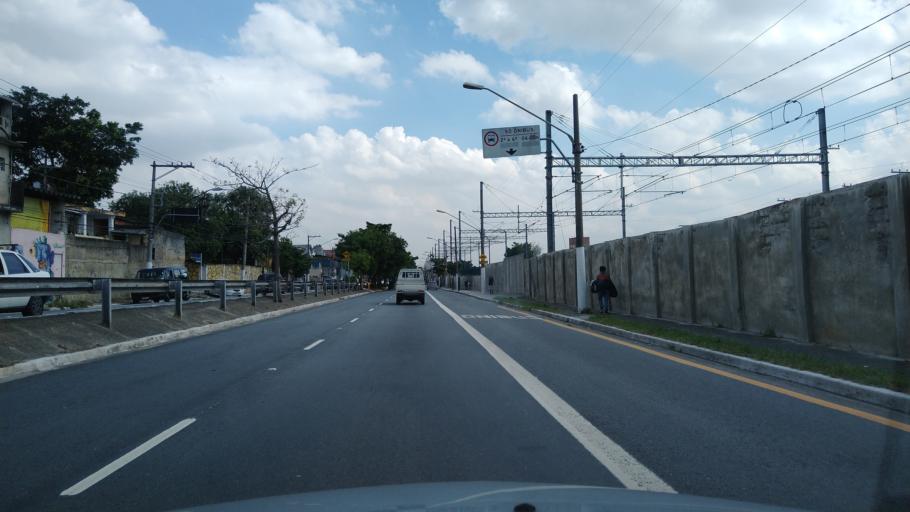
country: BR
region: Sao Paulo
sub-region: Guarulhos
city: Guarulhos
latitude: -23.5009
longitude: -46.5322
